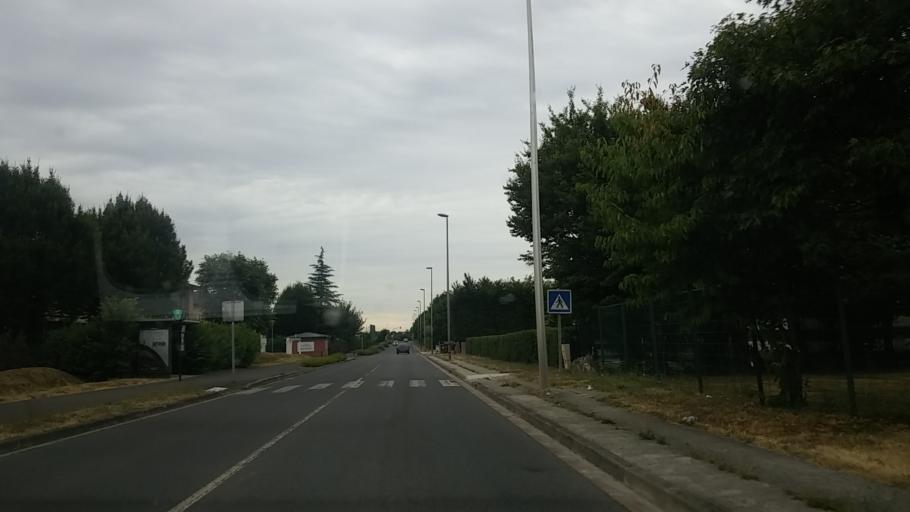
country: FR
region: Ile-de-France
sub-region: Departement de Seine-et-Marne
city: Champs-sur-Marne
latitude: 48.8304
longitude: 2.6035
